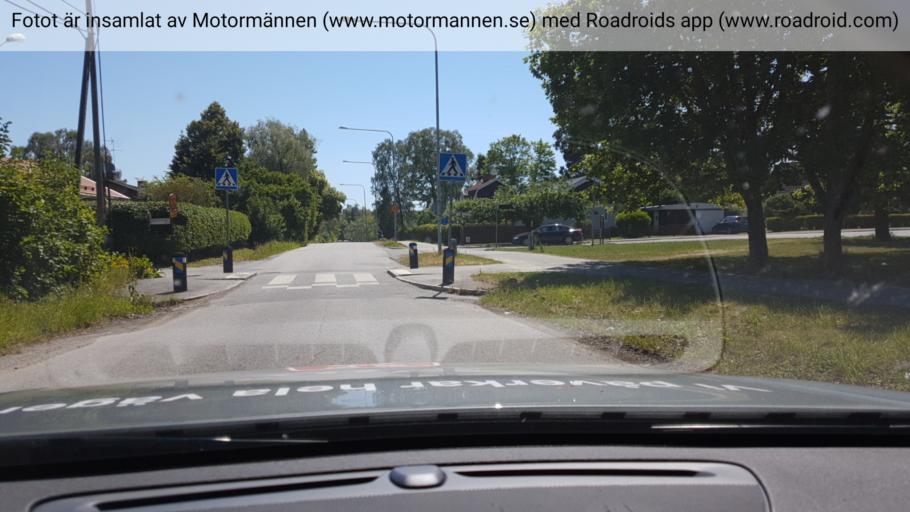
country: SE
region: Stockholm
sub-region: Huddinge Kommun
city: Huddinge
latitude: 59.2380
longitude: 17.9946
